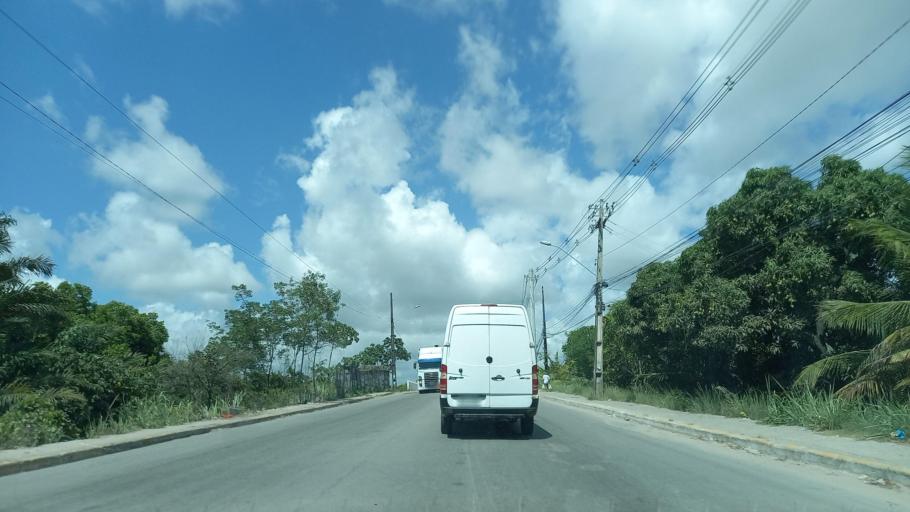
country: BR
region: Pernambuco
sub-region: Jaboatao Dos Guararapes
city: Jaboatao
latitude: -8.1551
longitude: -34.9492
